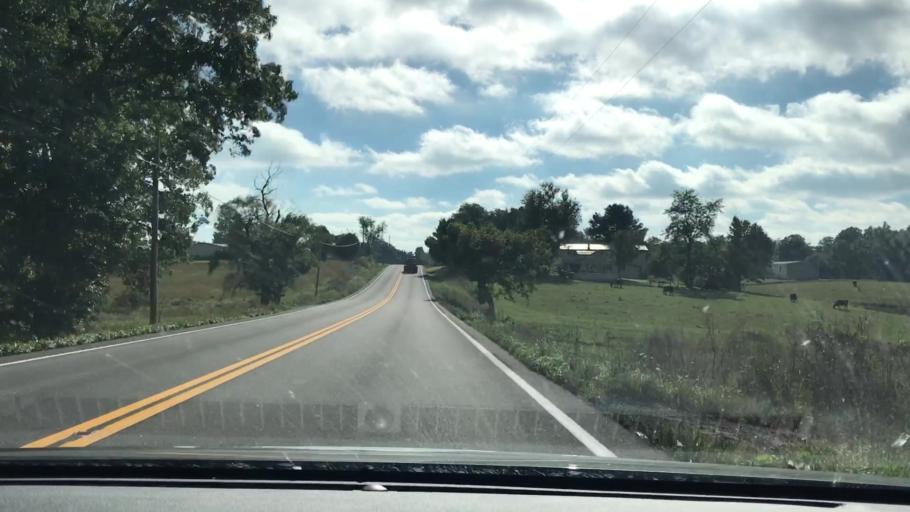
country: US
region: Tennessee
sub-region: Fentress County
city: Grimsley
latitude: 36.1685
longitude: -85.0604
